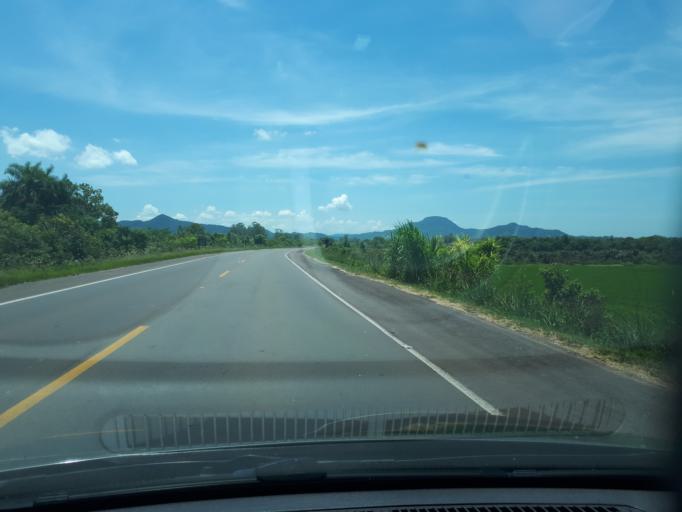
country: BR
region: Rio Grande do Sul
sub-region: Candelaria
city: Candelaria
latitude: -29.7301
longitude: -52.9427
